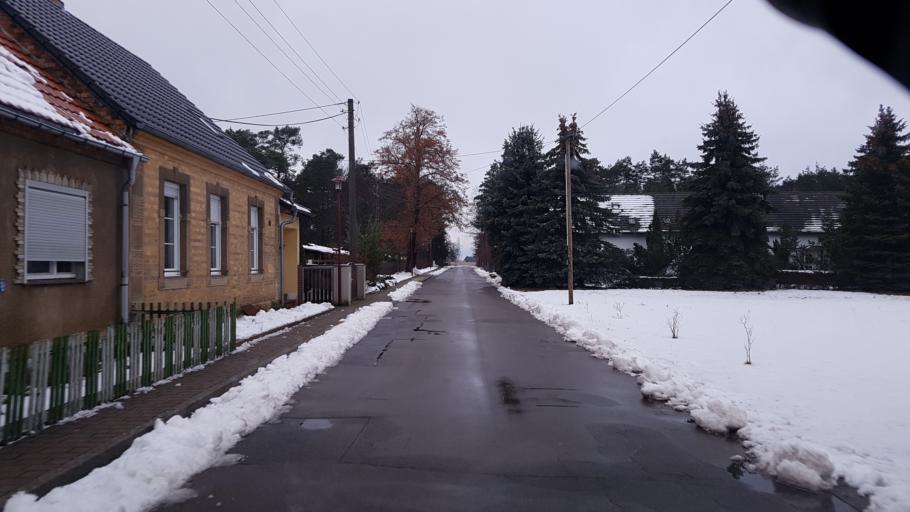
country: DE
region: Brandenburg
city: Luckau
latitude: 51.8622
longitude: 13.8133
